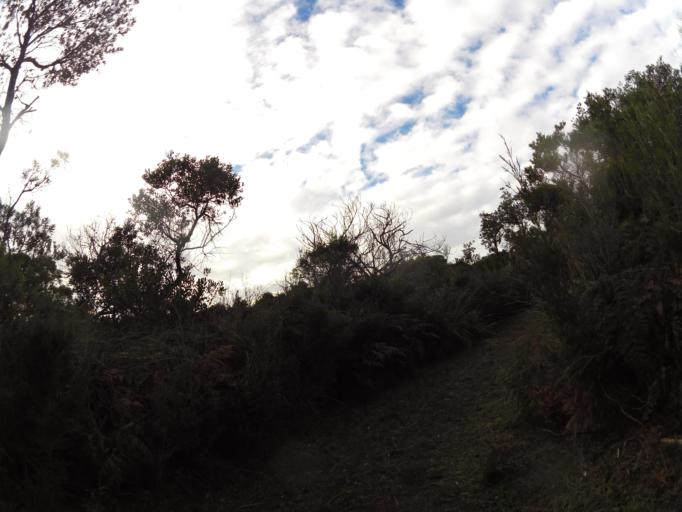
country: AU
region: Victoria
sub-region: Bass Coast
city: North Wonthaggi
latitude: -38.6403
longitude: 145.5611
